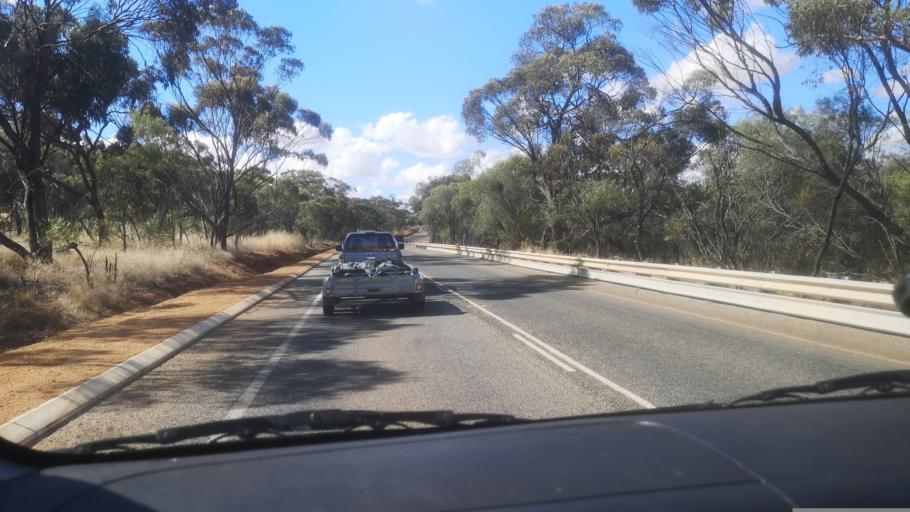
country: AU
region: Western Australia
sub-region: Toodyay
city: Toodyay
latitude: -31.5643
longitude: 116.4762
